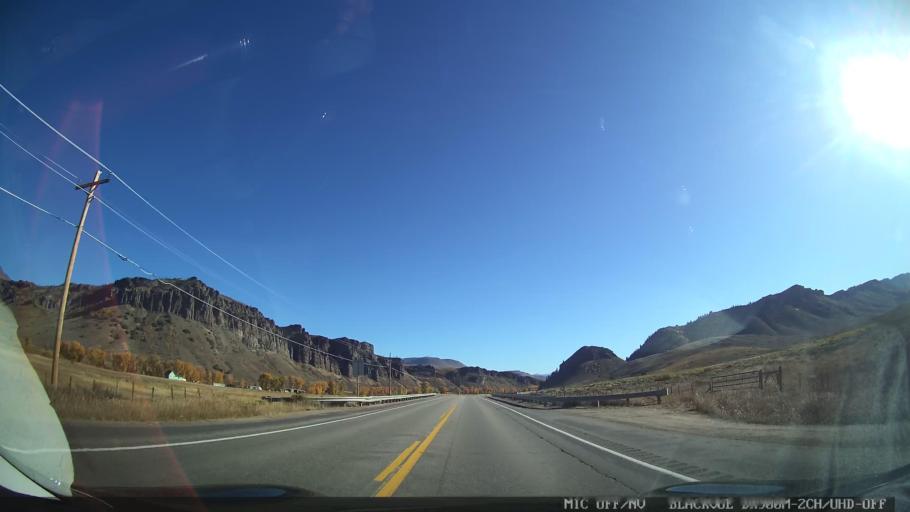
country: US
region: Colorado
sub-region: Grand County
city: Hot Sulphur Springs
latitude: 40.0789
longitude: -106.0912
